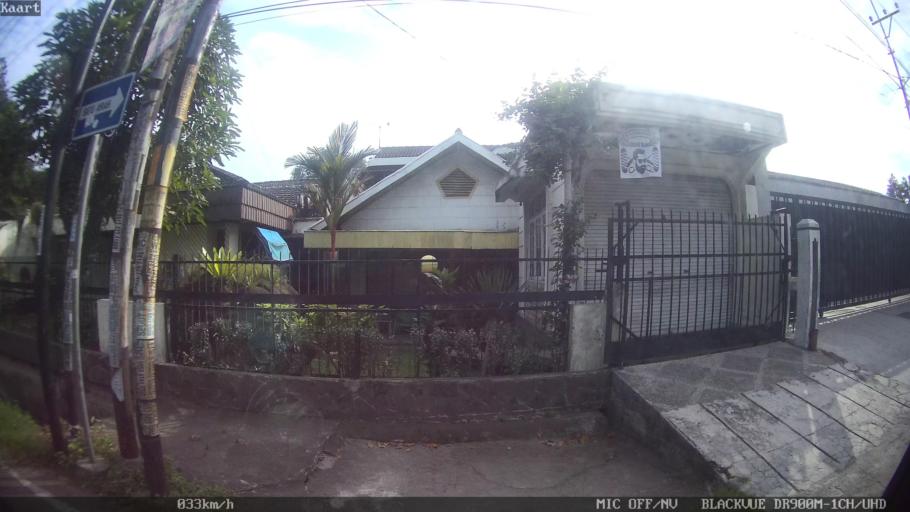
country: ID
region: Lampung
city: Bandarlampung
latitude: -5.4438
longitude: 105.2714
